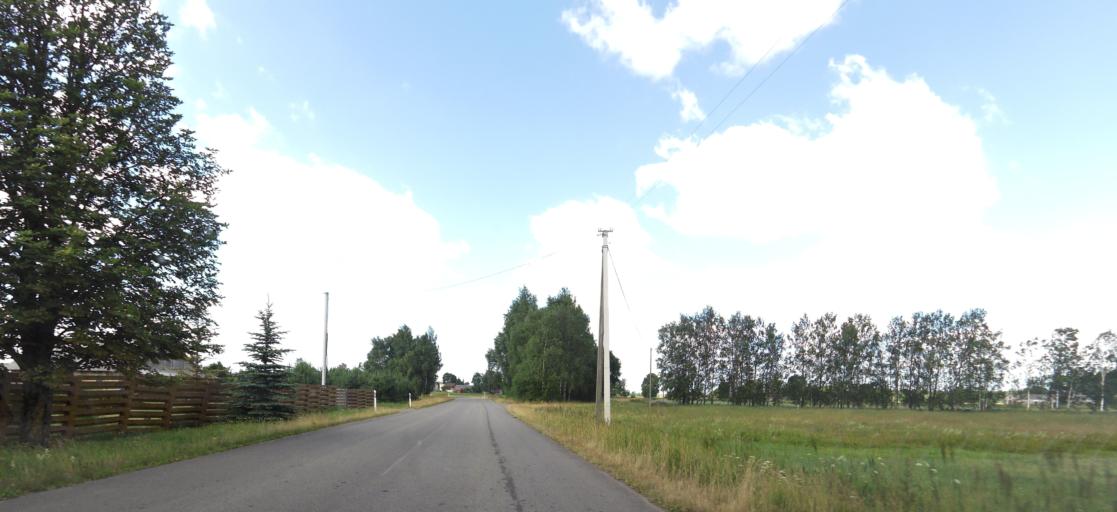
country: LT
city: Vabalninkas
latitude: 56.0317
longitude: 24.8125
